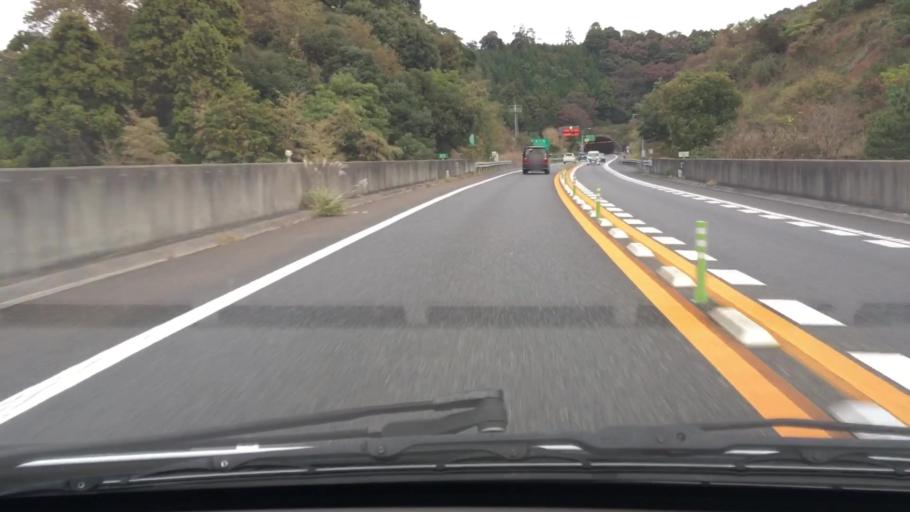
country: JP
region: Chiba
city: Futtsu
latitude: 35.1942
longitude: 139.8496
